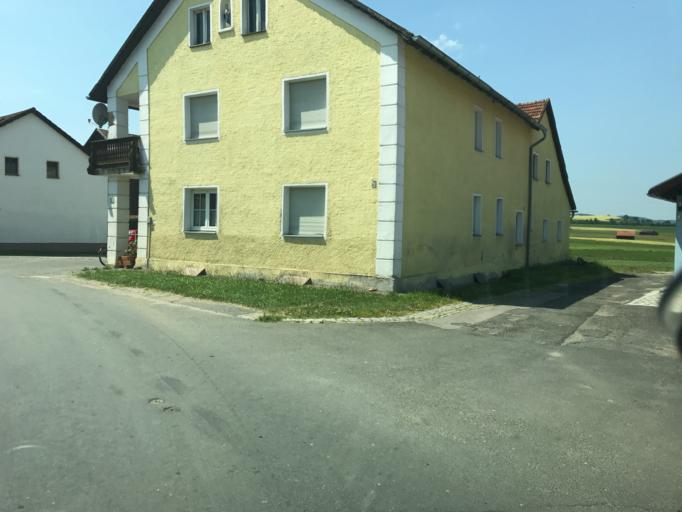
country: DE
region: Bavaria
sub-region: Upper Palatinate
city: Schonthal
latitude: 49.3392
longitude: 12.6312
